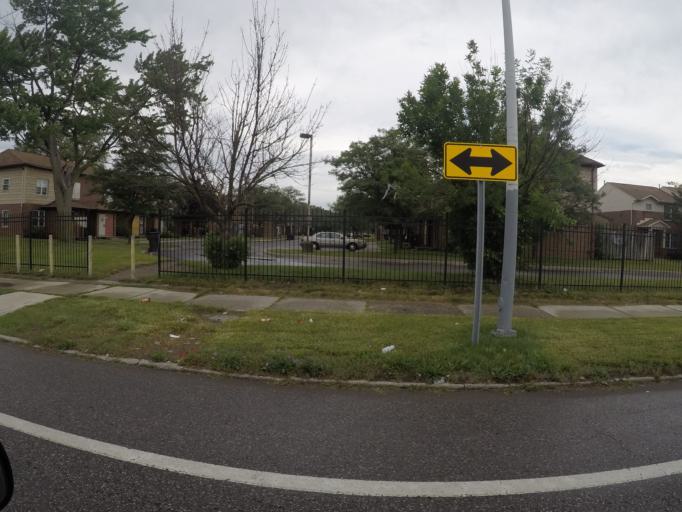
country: US
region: Michigan
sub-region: Wayne County
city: Grosse Pointe Park
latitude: 42.3919
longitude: -82.9692
